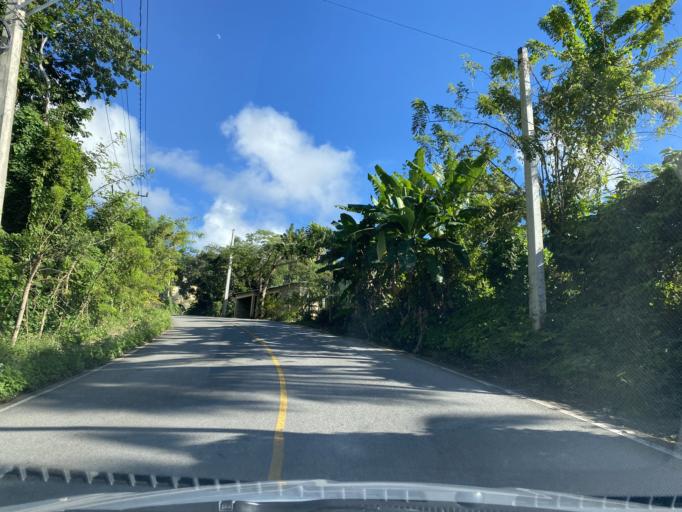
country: DO
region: Samana
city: Sanchez
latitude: 19.2550
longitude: -69.5773
